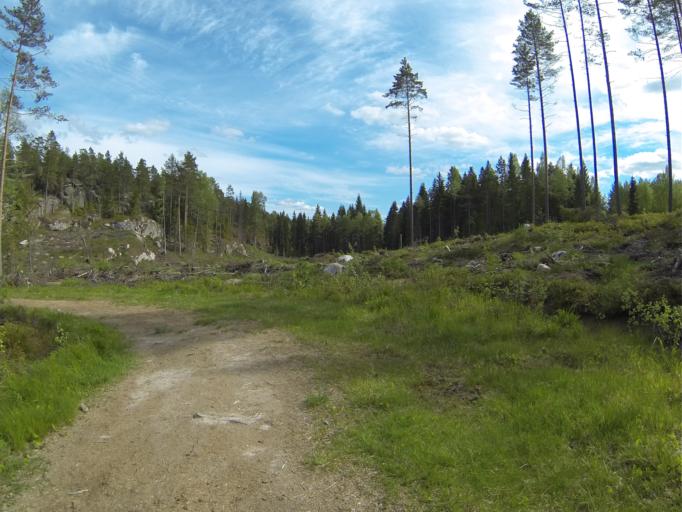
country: FI
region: Varsinais-Suomi
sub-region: Salo
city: Pertteli
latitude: 60.3842
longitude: 23.2131
